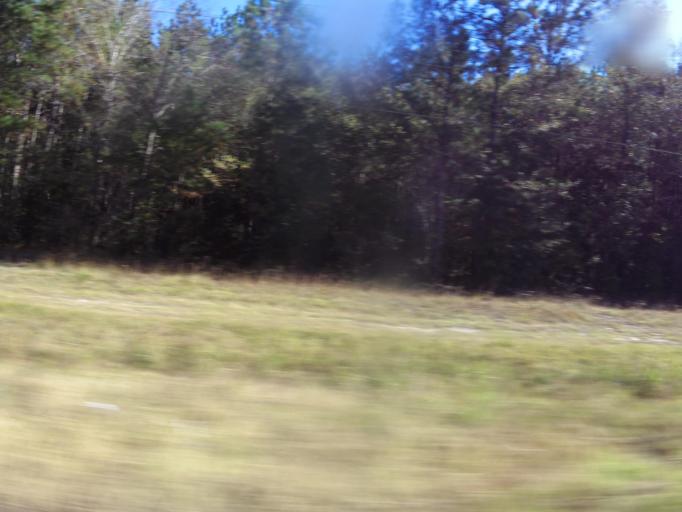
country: US
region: Georgia
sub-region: Liberty County
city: Midway
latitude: 31.8653
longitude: -81.3988
